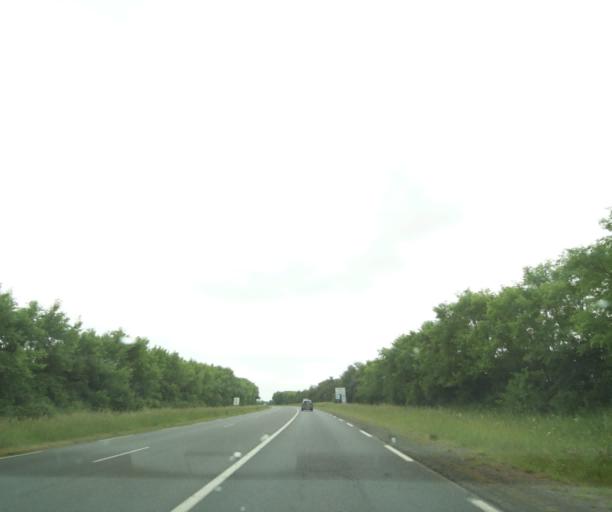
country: FR
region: Poitou-Charentes
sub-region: Departement des Deux-Sevres
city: Airvault
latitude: 46.8176
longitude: -0.2063
